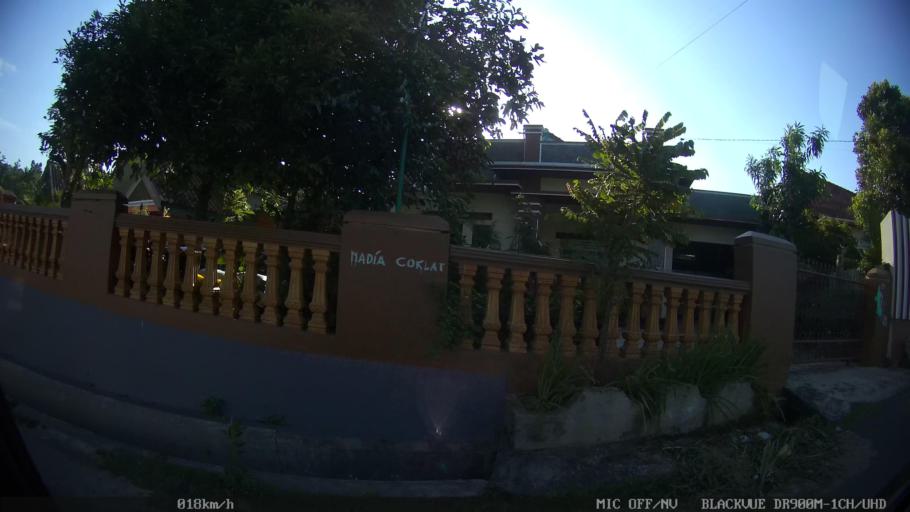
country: ID
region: Lampung
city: Kedaton
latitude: -5.3907
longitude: 105.2255
